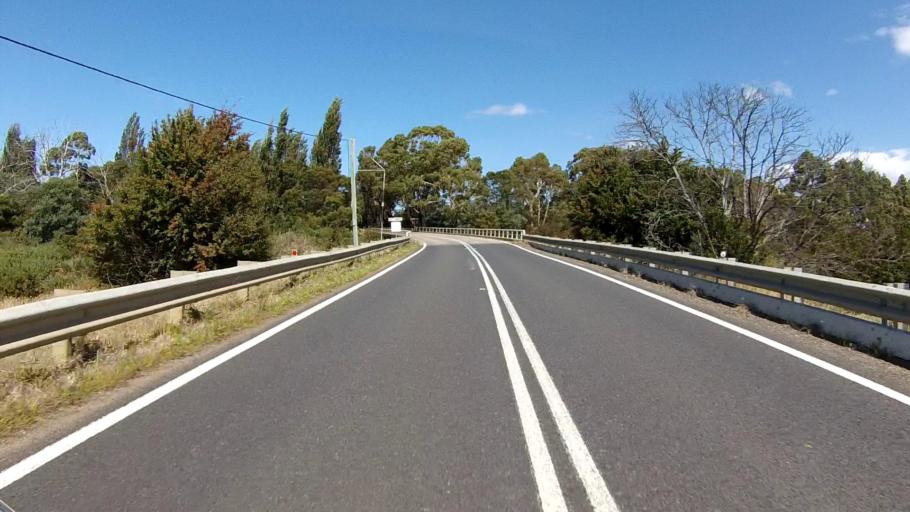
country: AU
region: Tasmania
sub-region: Break O'Day
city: St Helens
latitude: -42.0676
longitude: 148.0638
